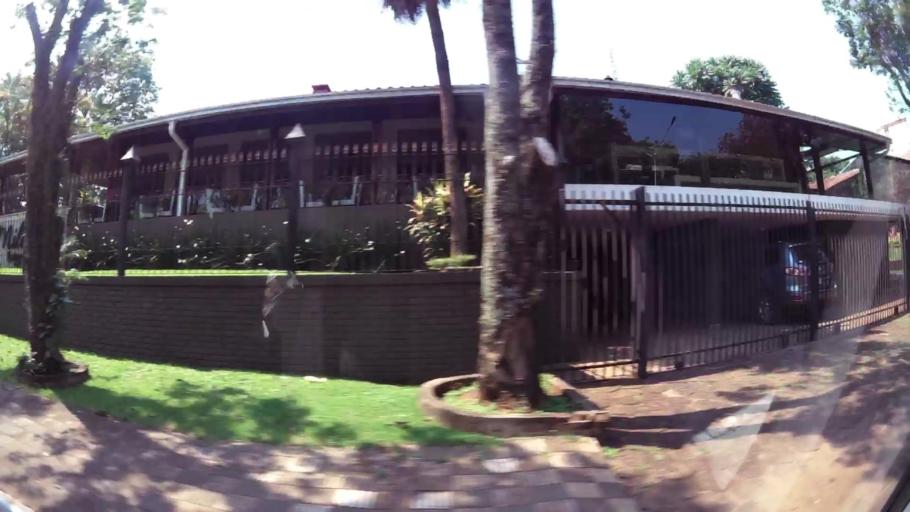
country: PY
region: Alto Parana
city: Ciudad del Este
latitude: -25.5196
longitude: -54.6215
